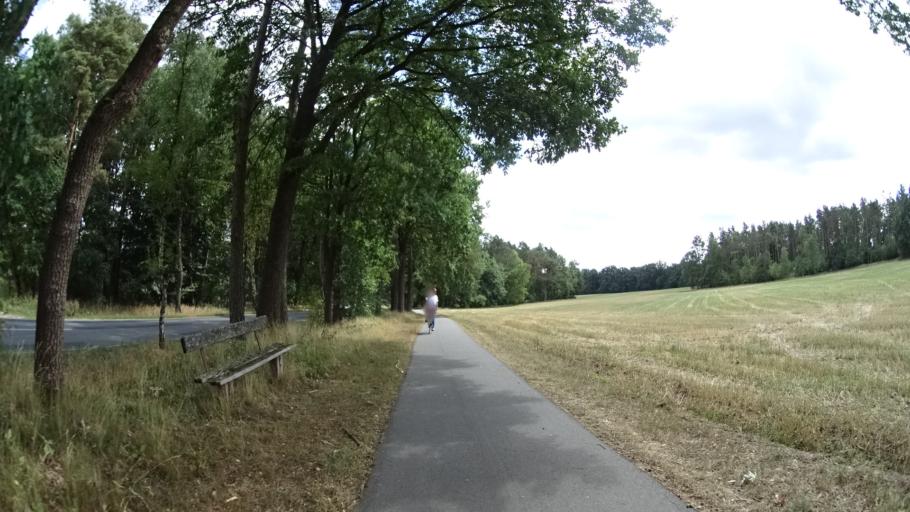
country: DE
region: Lower Saxony
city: Undeloh
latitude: 53.2004
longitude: 9.9667
